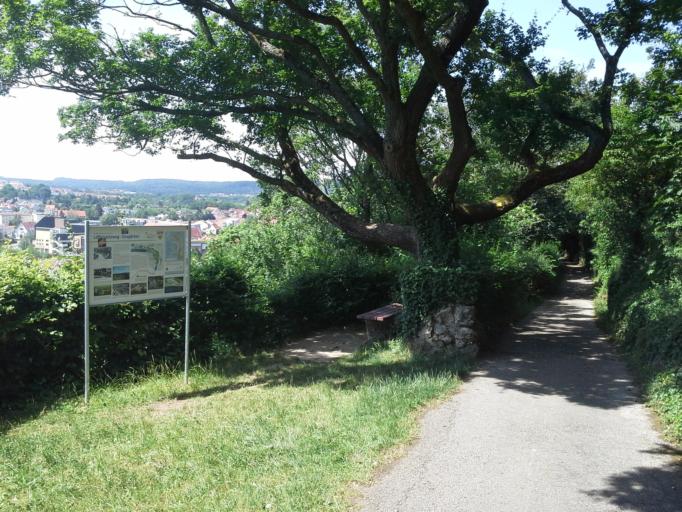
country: DE
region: Baden-Wuerttemberg
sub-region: Karlsruhe Region
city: Muhlacker
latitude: 48.9428
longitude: 8.8454
